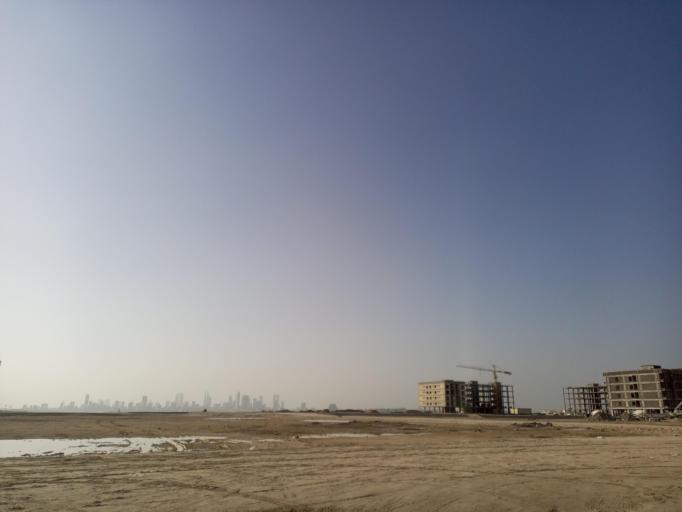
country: BH
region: Muharraq
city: Al Hadd
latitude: 26.2284
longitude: 50.6449
